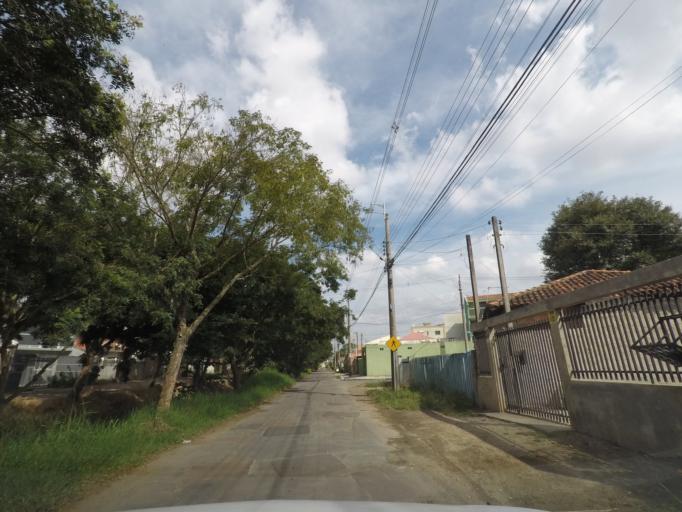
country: BR
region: Parana
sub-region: Pinhais
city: Pinhais
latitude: -25.4835
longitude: -49.1968
